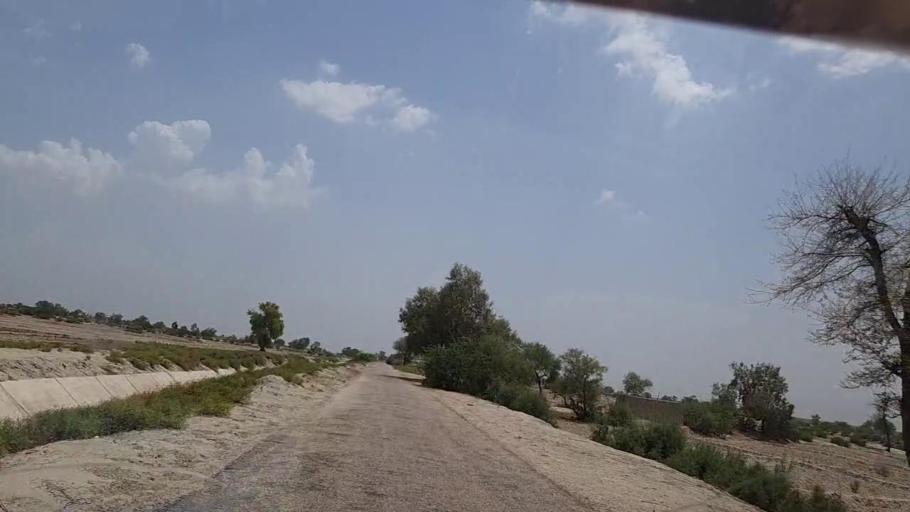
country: PK
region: Sindh
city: Bhan
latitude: 26.5369
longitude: 67.6331
